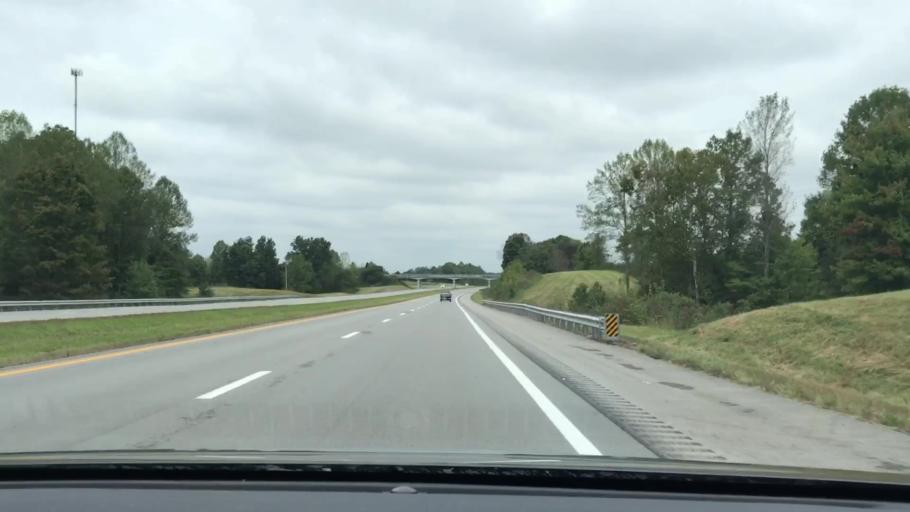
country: US
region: Kentucky
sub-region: Russell County
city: Russell Springs
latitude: 37.0522
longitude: -85.1593
